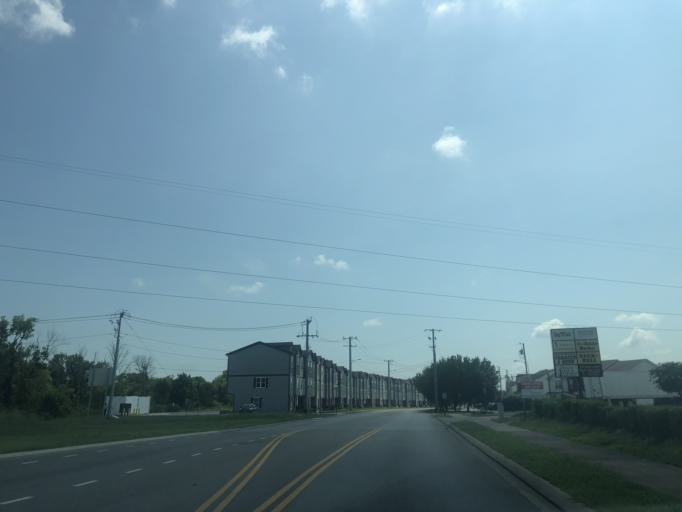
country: US
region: Tennessee
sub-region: Rutherford County
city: La Vergne
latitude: 36.0253
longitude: -86.5853
